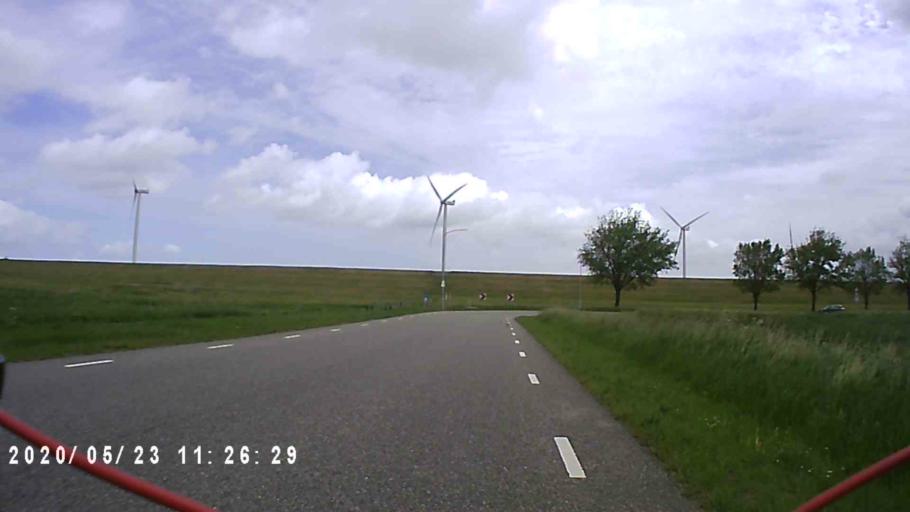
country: NL
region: Groningen
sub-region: Gemeente Delfzijl
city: Delfzijl
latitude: 53.3112
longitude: 6.9922
